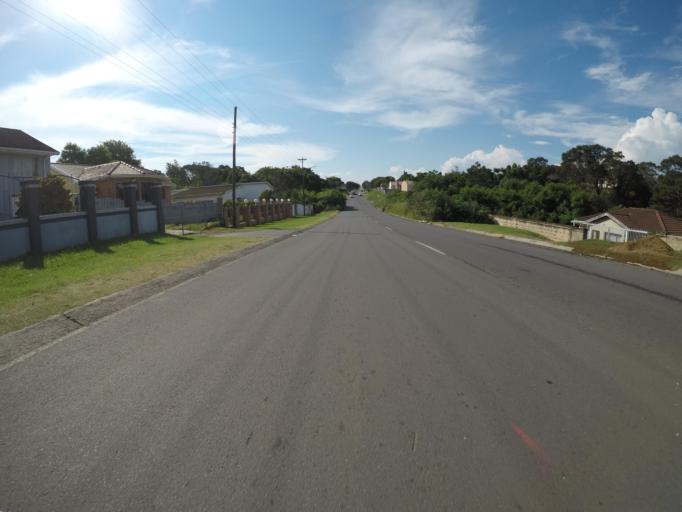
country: ZA
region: Eastern Cape
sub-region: Buffalo City Metropolitan Municipality
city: East London
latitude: -32.9979
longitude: 27.8505
